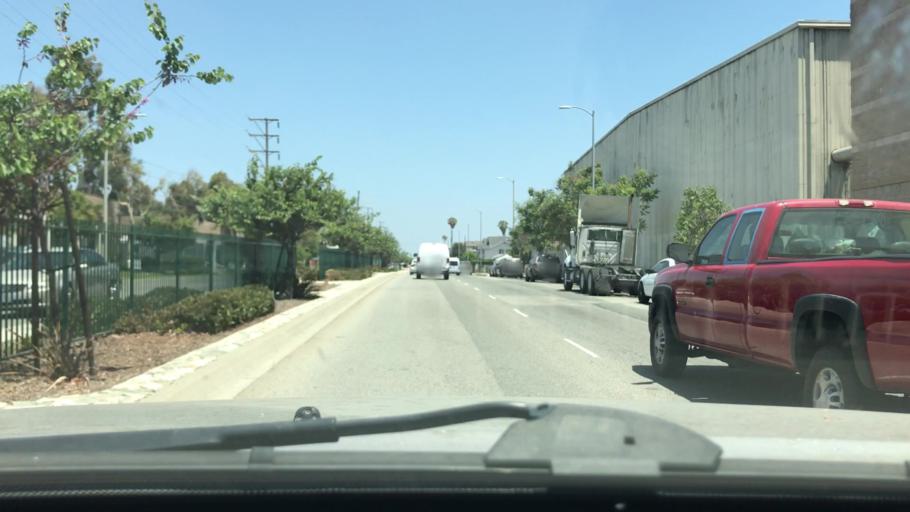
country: US
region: California
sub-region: Los Angeles County
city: West Carson
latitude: 33.8396
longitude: -118.3092
